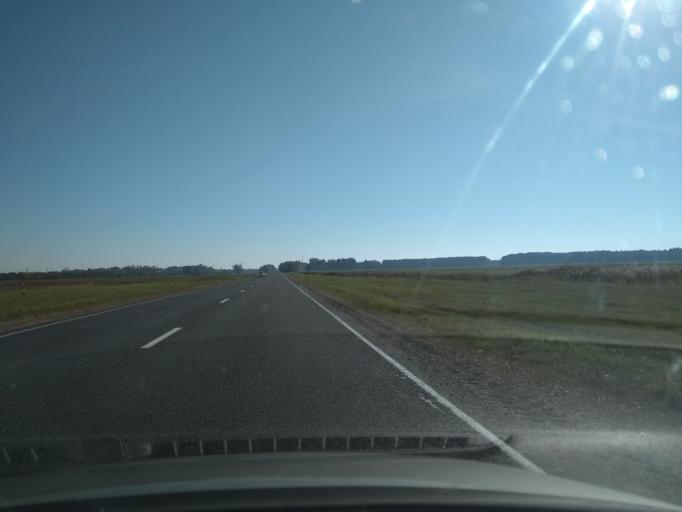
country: BY
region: Brest
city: Malaryta
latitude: 51.9410
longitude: 24.0337
